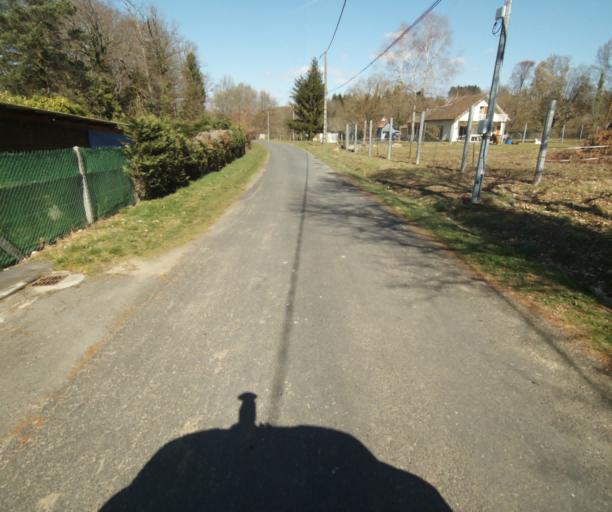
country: FR
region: Limousin
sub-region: Departement de la Correze
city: Saint-Mexant
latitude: 45.2896
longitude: 1.6688
